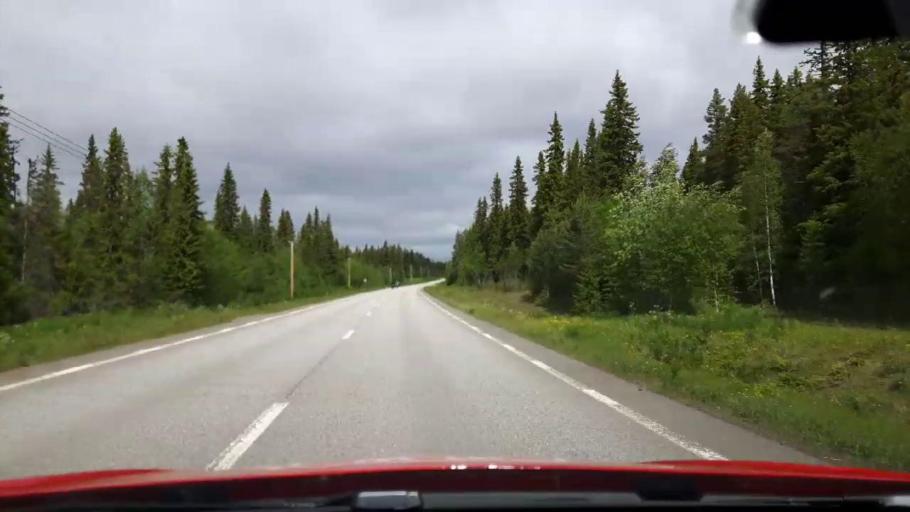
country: SE
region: Jaemtland
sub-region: Krokoms Kommun
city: Krokom
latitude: 63.4844
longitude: 14.5049
